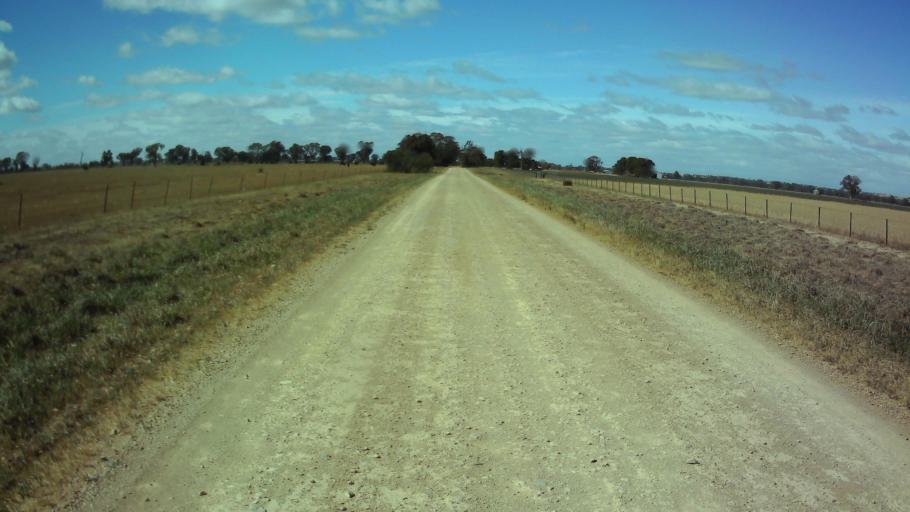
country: AU
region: New South Wales
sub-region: Weddin
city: Grenfell
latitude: -34.0232
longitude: 148.3187
